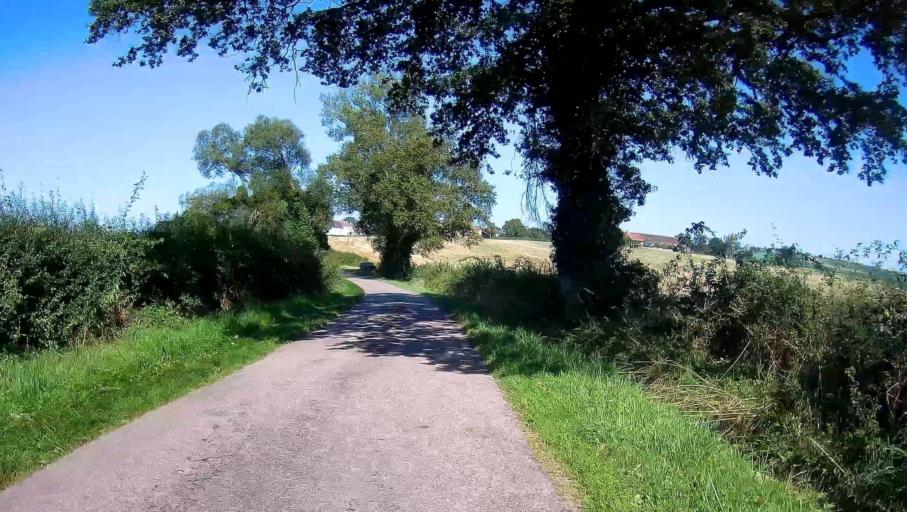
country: FR
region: Bourgogne
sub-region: Departement de Saone-et-Loire
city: Couches
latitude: 46.8339
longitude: 4.5915
